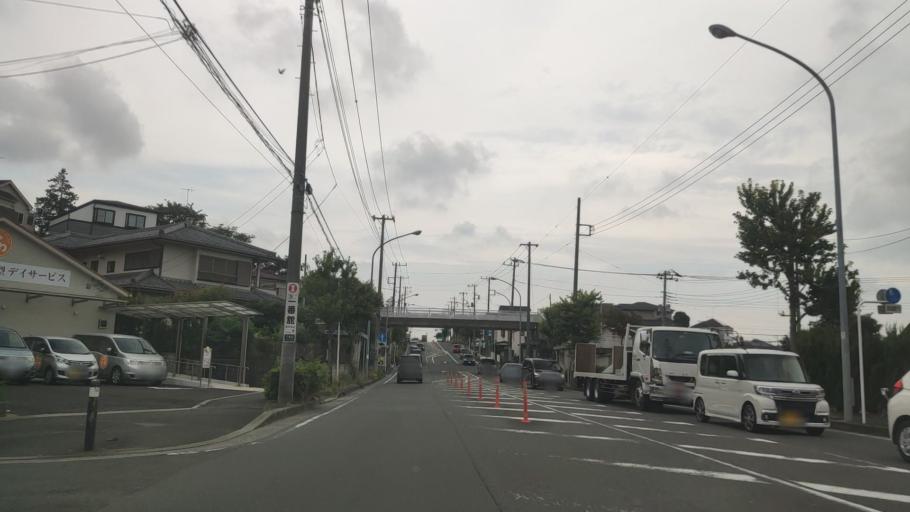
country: JP
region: Kanagawa
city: Minami-rinkan
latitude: 35.4527
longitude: 139.4828
